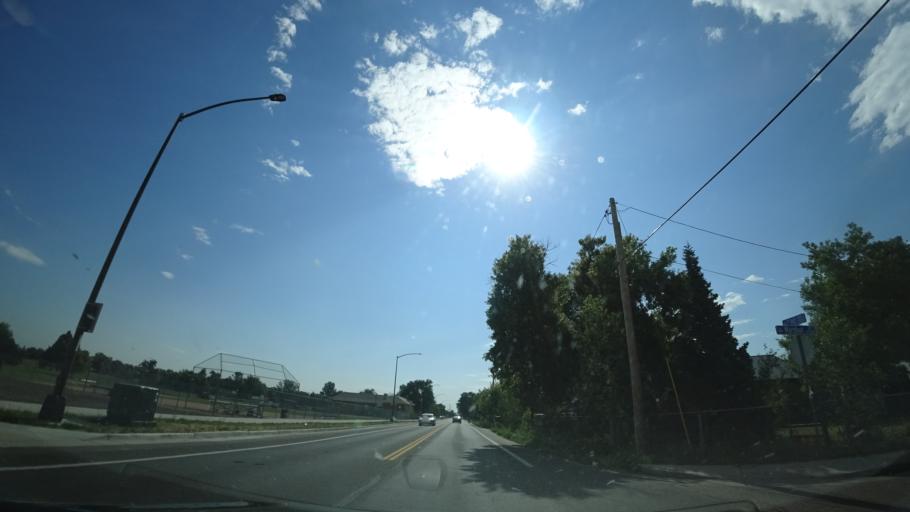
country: US
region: Colorado
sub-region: Jefferson County
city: Lakewood
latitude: 39.7185
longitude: -105.0688
